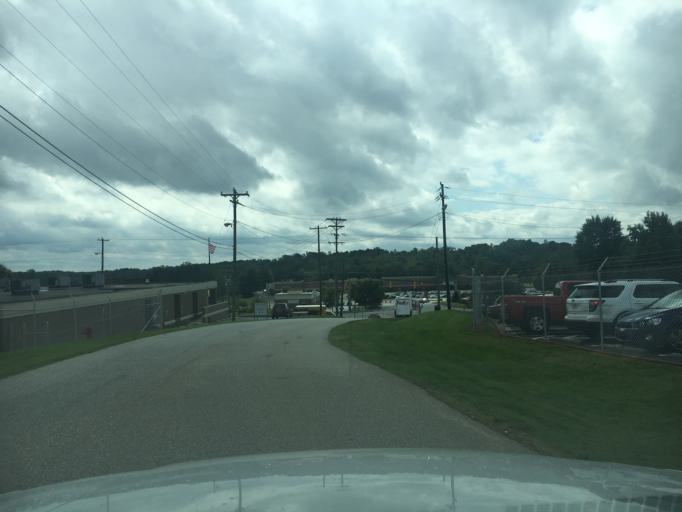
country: US
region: North Carolina
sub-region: Catawba County
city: Conover
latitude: 35.7001
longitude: -81.2796
